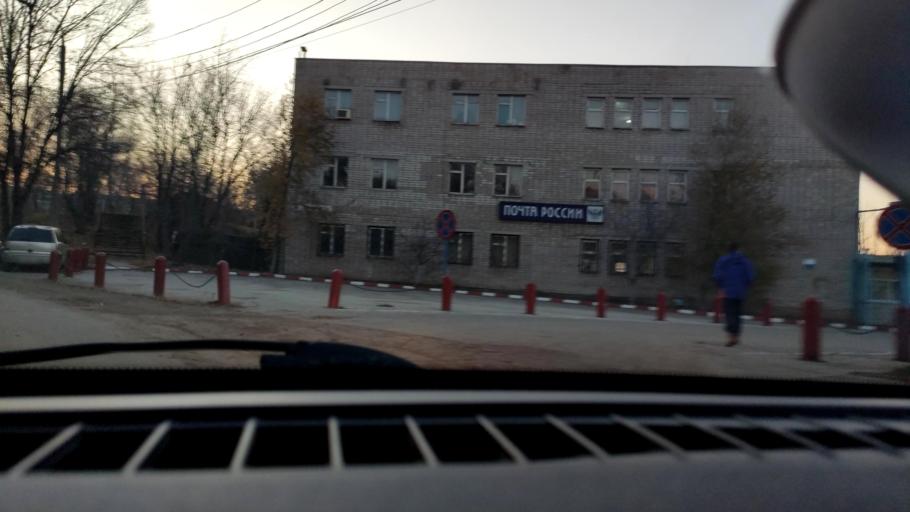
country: RU
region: Samara
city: Samara
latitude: 53.1806
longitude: 50.1121
